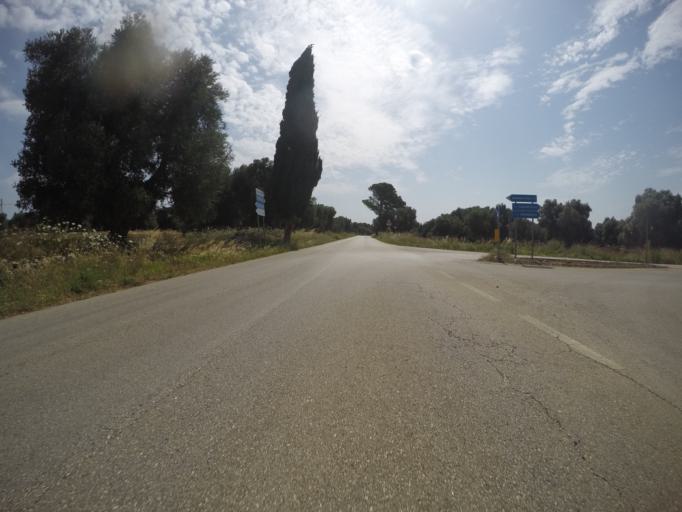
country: IT
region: Apulia
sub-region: Provincia di Brindisi
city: Francavilla Fontana
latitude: 40.5489
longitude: 17.5385
